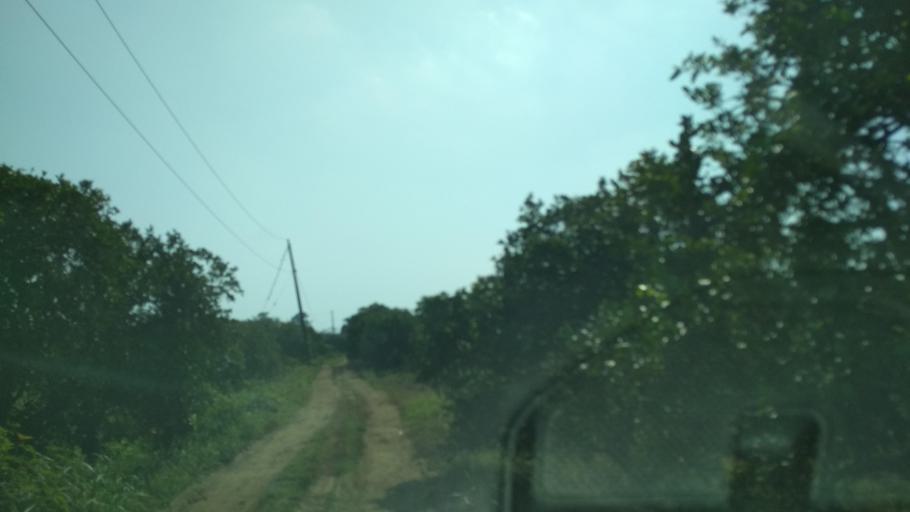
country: MX
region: Puebla
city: San Jose Acateno
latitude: 20.2052
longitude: -97.1826
